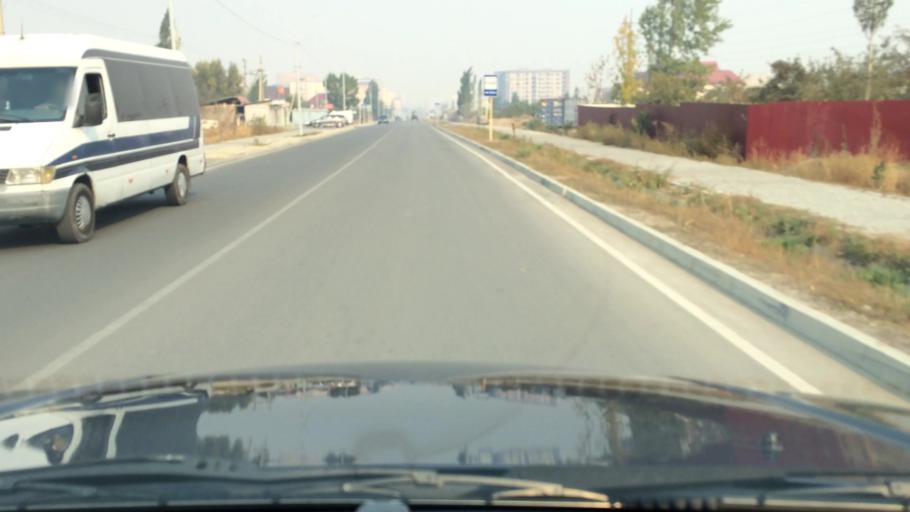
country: KG
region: Chuy
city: Bishkek
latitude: 42.8240
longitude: 74.5698
